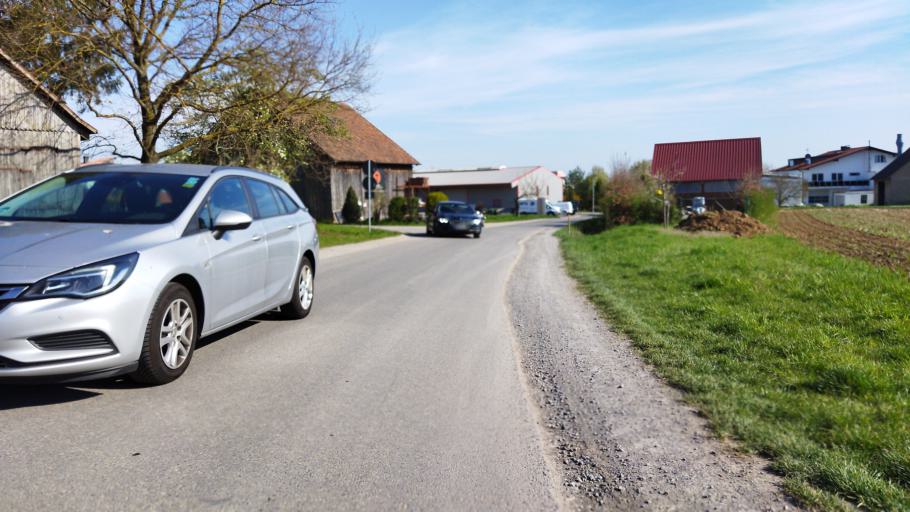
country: DE
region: Baden-Wuerttemberg
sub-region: Regierungsbezirk Stuttgart
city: Freudental
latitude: 48.9747
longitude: 9.0691
